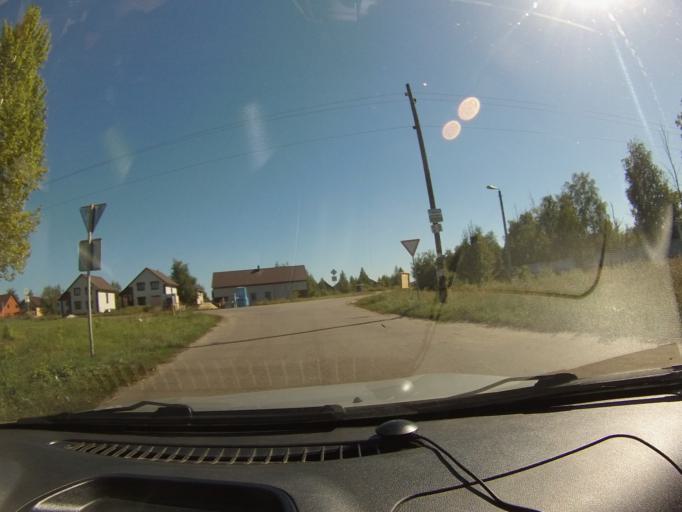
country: RU
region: Tambov
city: Komsomolets
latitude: 52.7688
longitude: 41.3613
